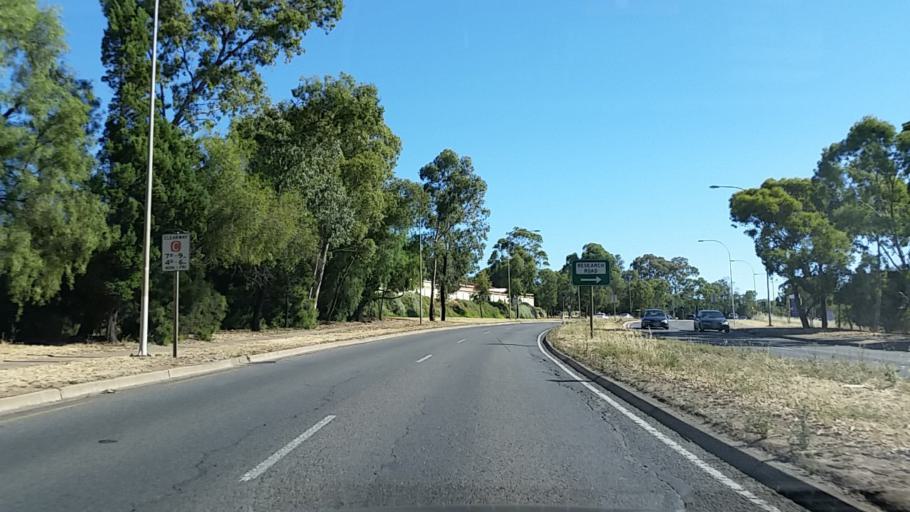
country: AU
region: South Australia
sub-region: Salisbury
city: Ingle Farm
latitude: -34.8177
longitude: 138.6412
